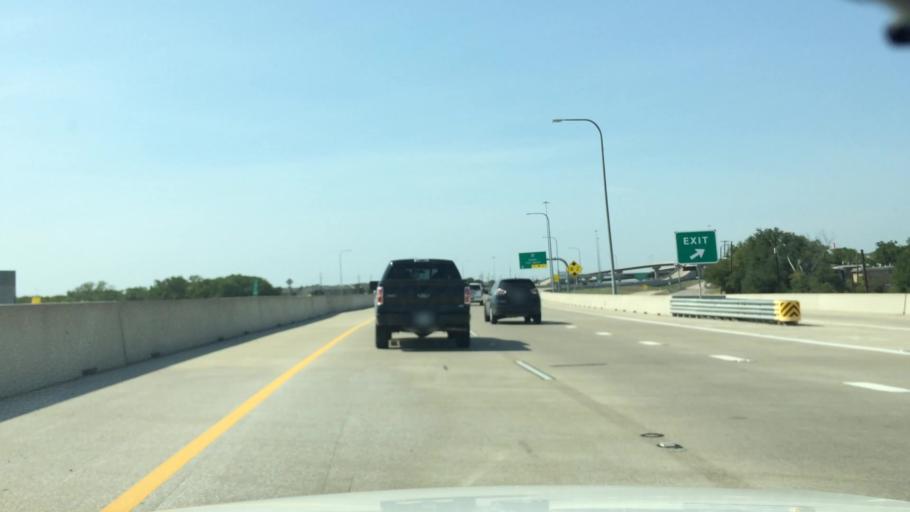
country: US
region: Texas
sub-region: Dallas County
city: Grand Prairie
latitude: 32.7504
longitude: -97.0277
